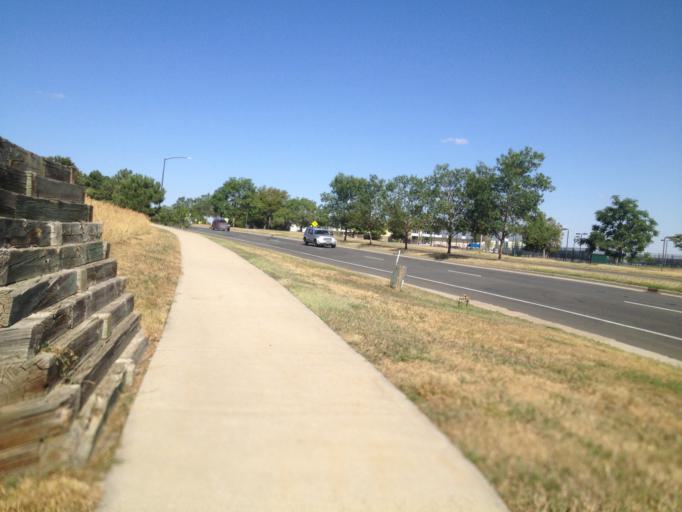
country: US
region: Colorado
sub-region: Boulder County
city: Superior
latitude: 39.9744
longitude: -105.1609
